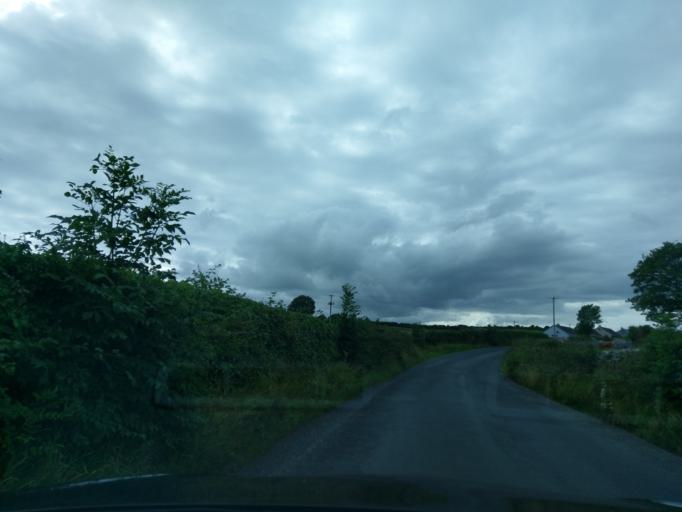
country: IE
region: Connaught
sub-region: County Galway
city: Loughrea
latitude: 53.1739
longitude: -8.6914
